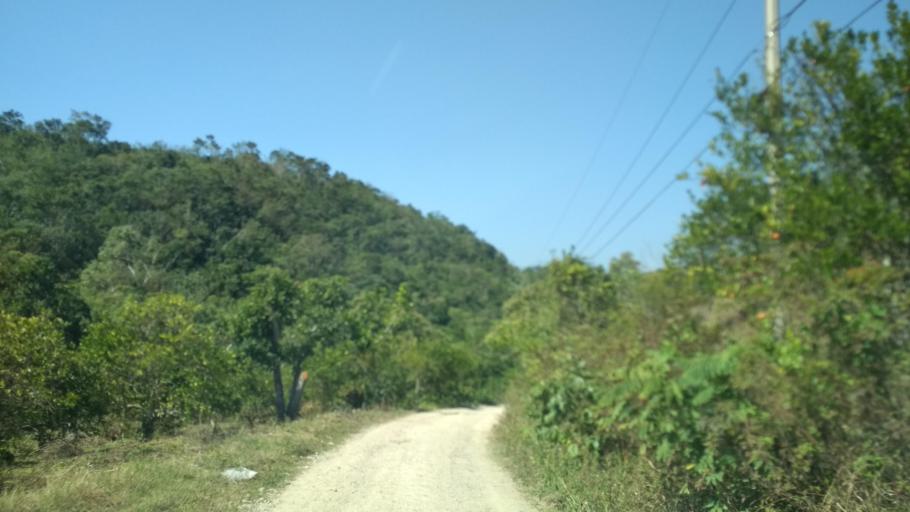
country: MX
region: Veracruz
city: Gutierrez Zamora
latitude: 20.4747
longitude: -97.1562
